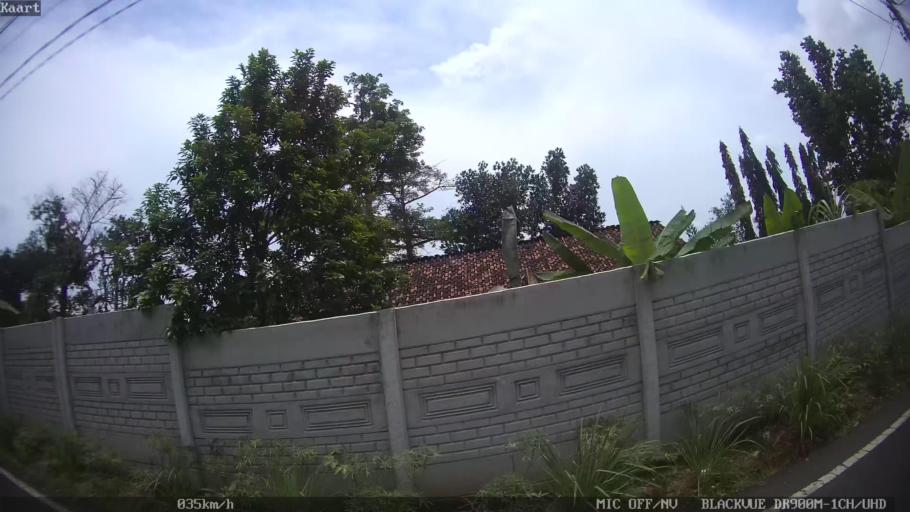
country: ID
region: Lampung
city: Bandarlampung
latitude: -5.4135
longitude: 105.2340
